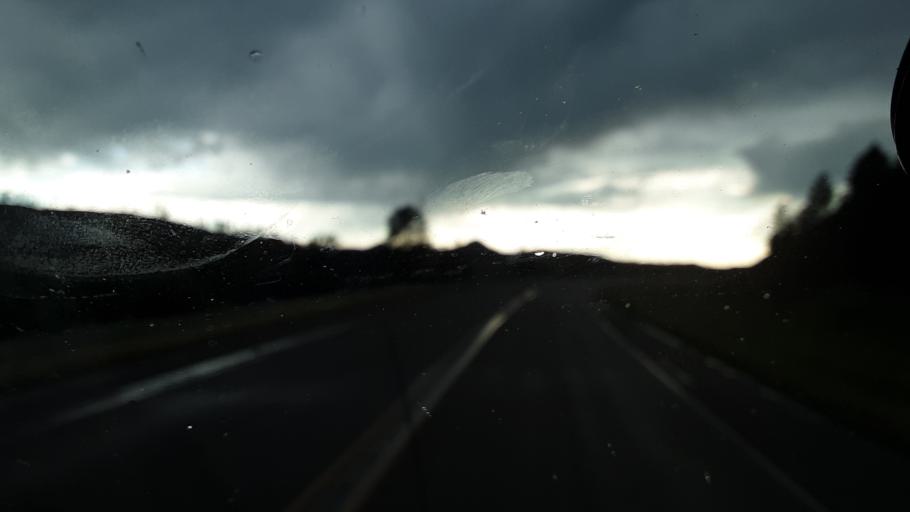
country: US
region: Montana
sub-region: Powder River County
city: Broadus
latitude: 45.5511
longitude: -105.9301
